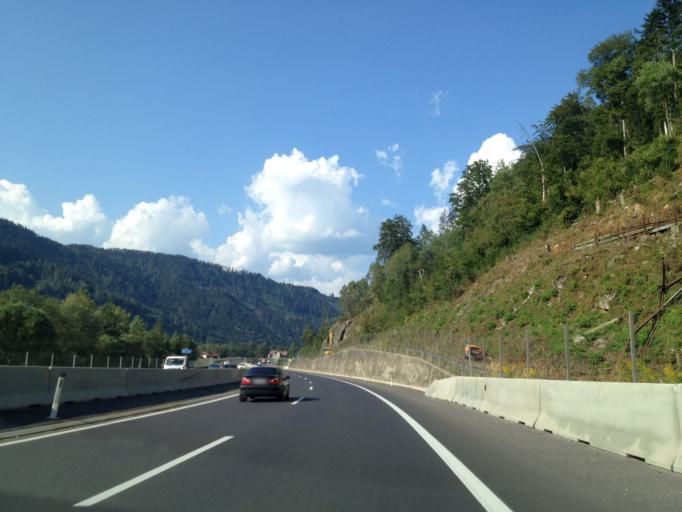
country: AT
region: Styria
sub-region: Politischer Bezirk Leoben
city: Leoben
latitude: 47.3427
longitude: 15.0553
